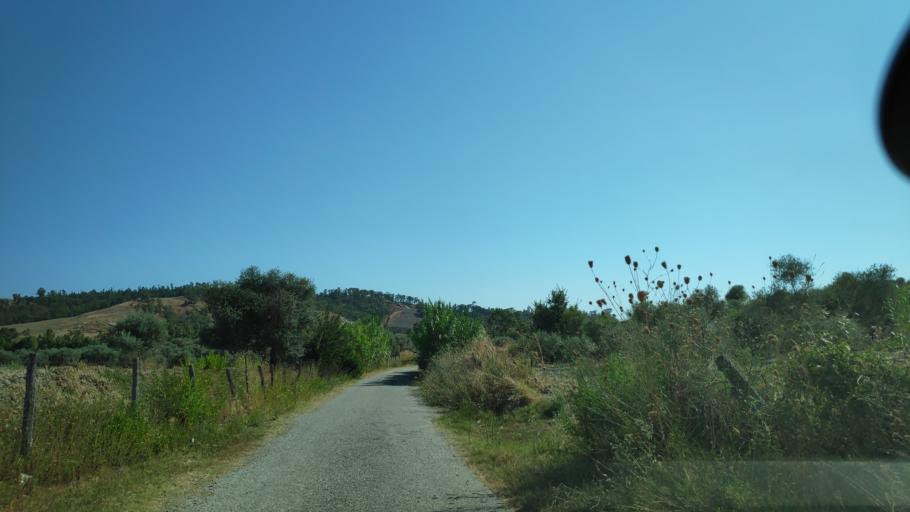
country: IT
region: Calabria
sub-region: Provincia di Reggio Calabria
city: Monasterace
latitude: 38.4313
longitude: 16.5249
